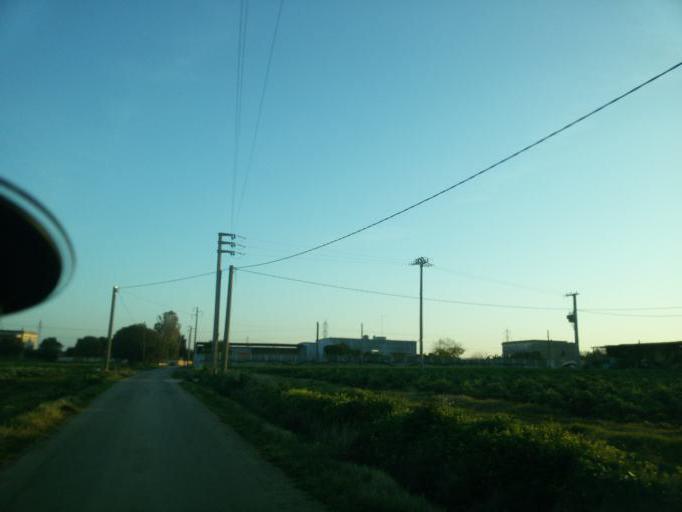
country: IT
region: Apulia
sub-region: Provincia di Brindisi
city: La Rosa
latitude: 40.6042
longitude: 17.9393
